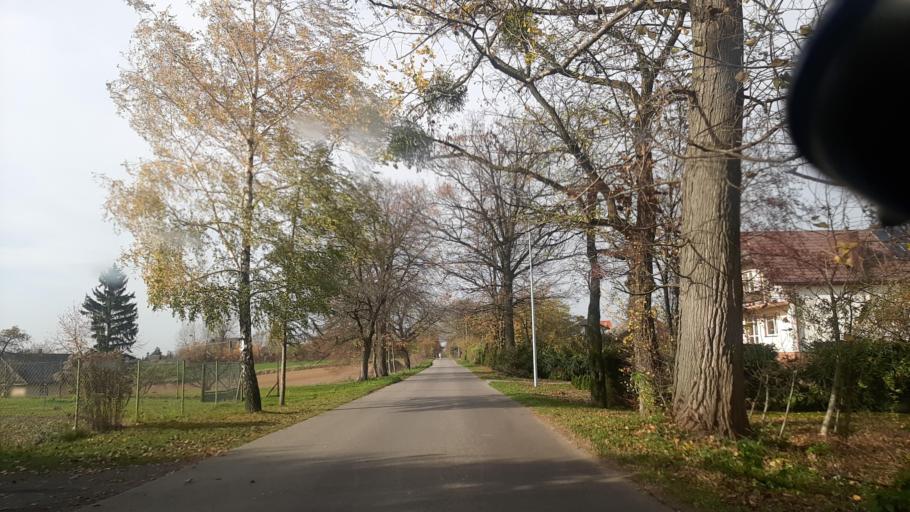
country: PL
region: Lublin Voivodeship
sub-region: Powiat lubelski
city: Jastkow
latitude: 51.3367
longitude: 22.4290
